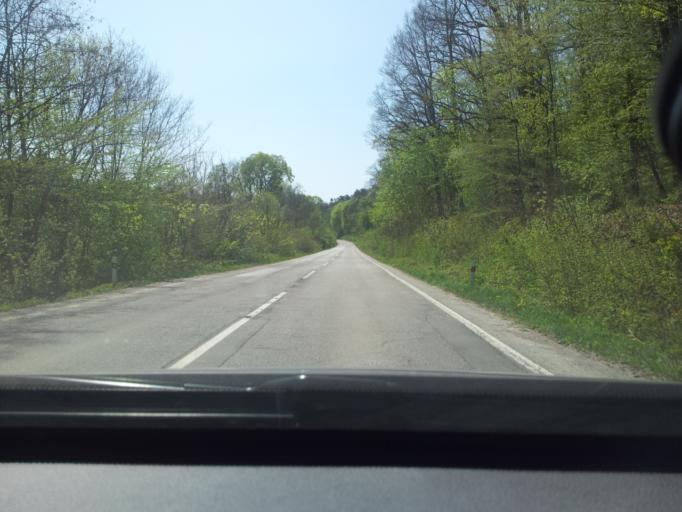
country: SK
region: Nitriansky
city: Zlate Moravce
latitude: 48.4423
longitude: 18.4104
